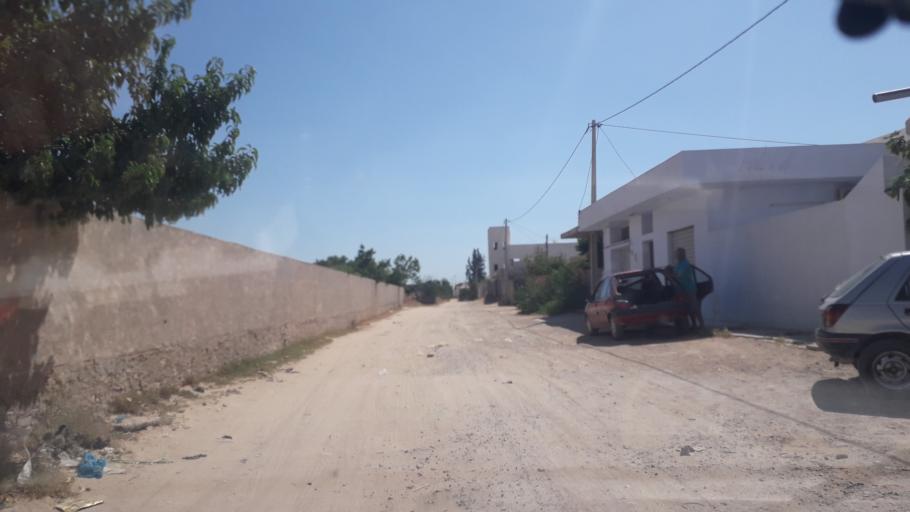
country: TN
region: Safaqis
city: Al Qarmadah
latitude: 34.8318
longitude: 10.7653
